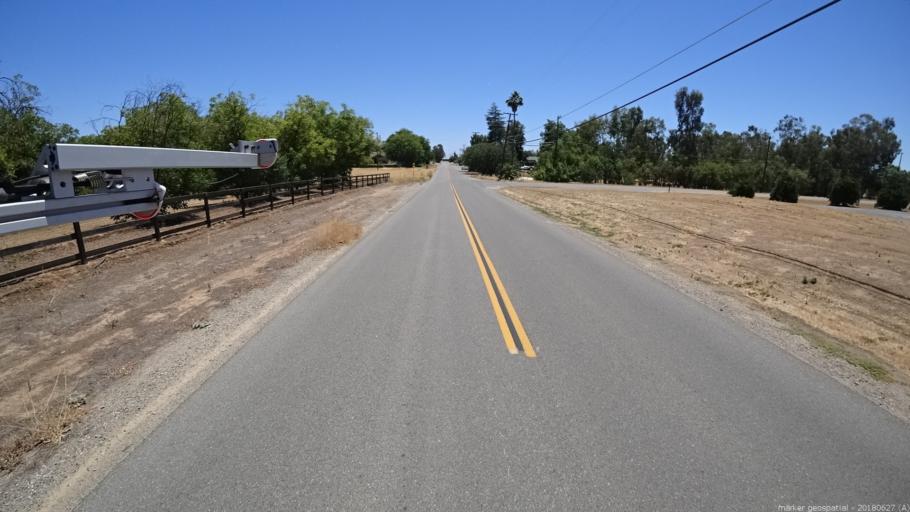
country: US
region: California
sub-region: Madera County
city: Bonadelle Ranchos-Madera Ranchos
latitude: 36.9289
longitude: -119.8625
